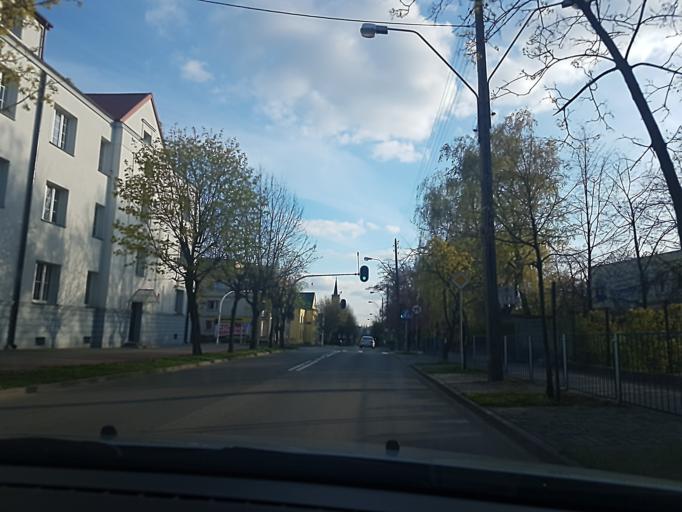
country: PL
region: Lodz Voivodeship
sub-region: Powiat kutnowski
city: Kutno
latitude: 52.2343
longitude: 19.3655
